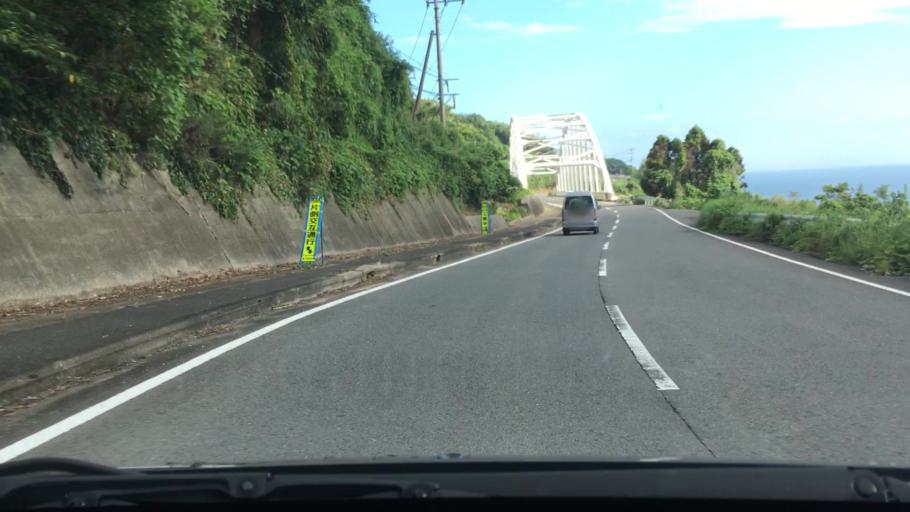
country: JP
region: Nagasaki
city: Togitsu
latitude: 32.8587
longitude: 129.6856
